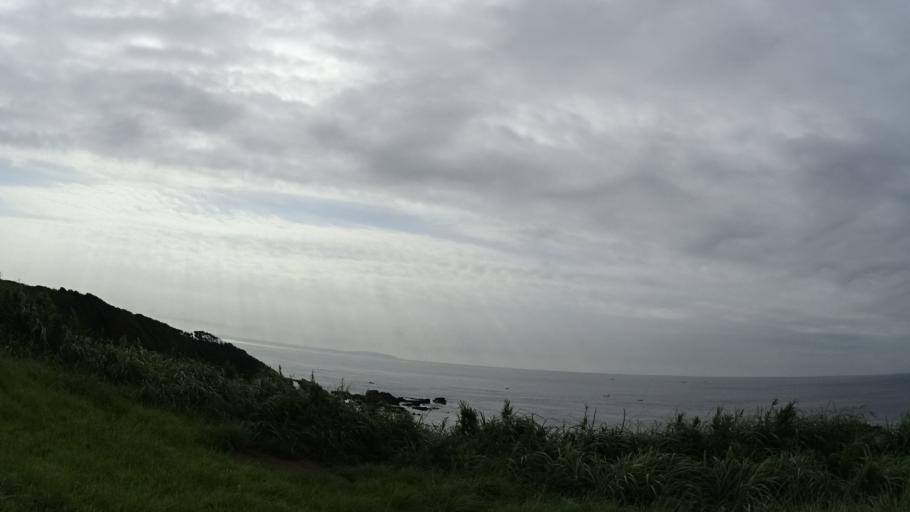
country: JP
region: Kanagawa
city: Miura
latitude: 35.1334
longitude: 139.6156
